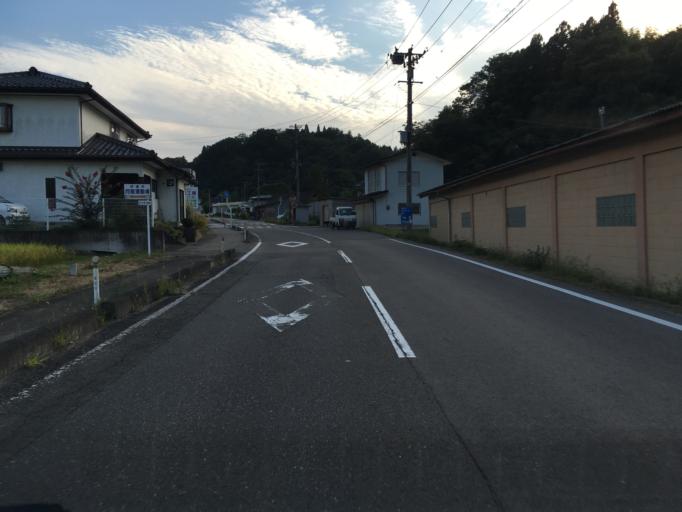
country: JP
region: Fukushima
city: Hobaramachi
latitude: 37.7187
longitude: 140.5917
